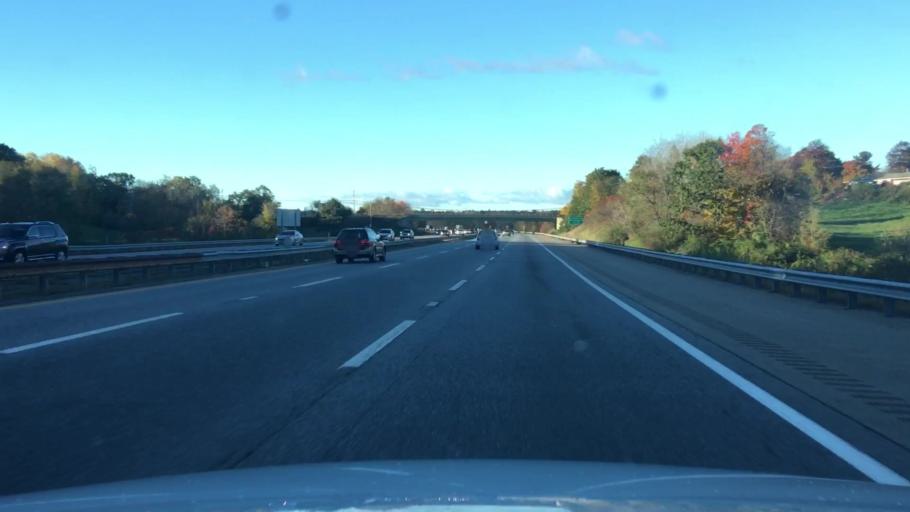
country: US
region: Maine
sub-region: York County
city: Biddeford
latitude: 43.5059
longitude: -70.4815
